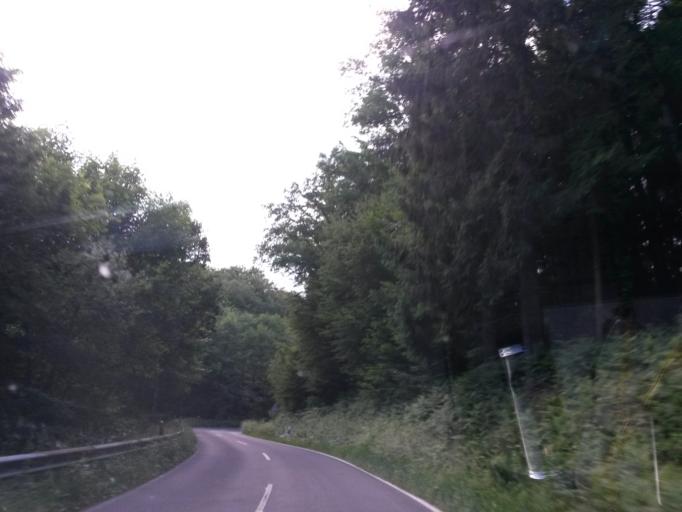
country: DE
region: North Rhine-Westphalia
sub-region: Regierungsbezirk Koln
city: Overath
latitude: 50.8856
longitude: 7.2988
